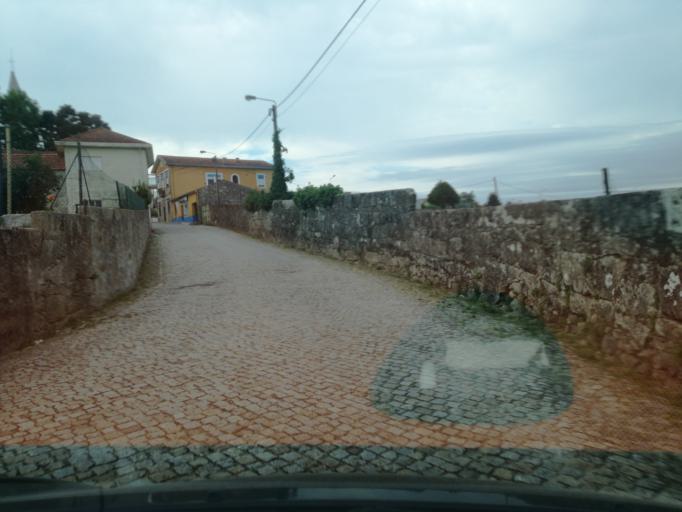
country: PT
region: Porto
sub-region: Maia
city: Maia
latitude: 41.2418
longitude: -8.6060
